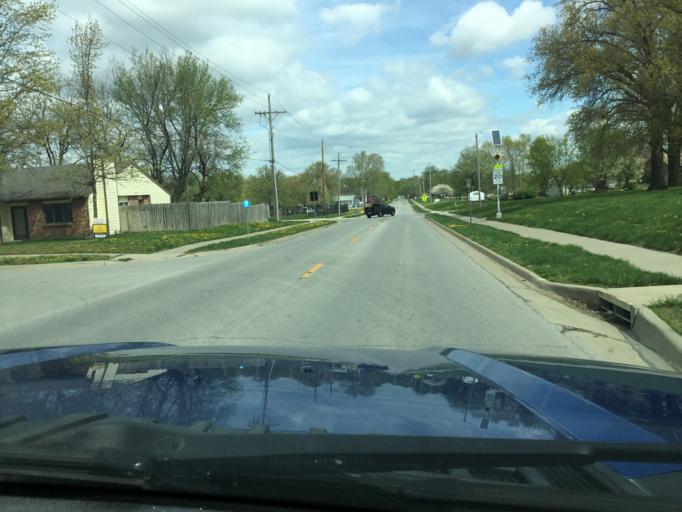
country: US
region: Kansas
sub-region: Douglas County
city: Lawrence
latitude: 38.9458
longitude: -95.2141
